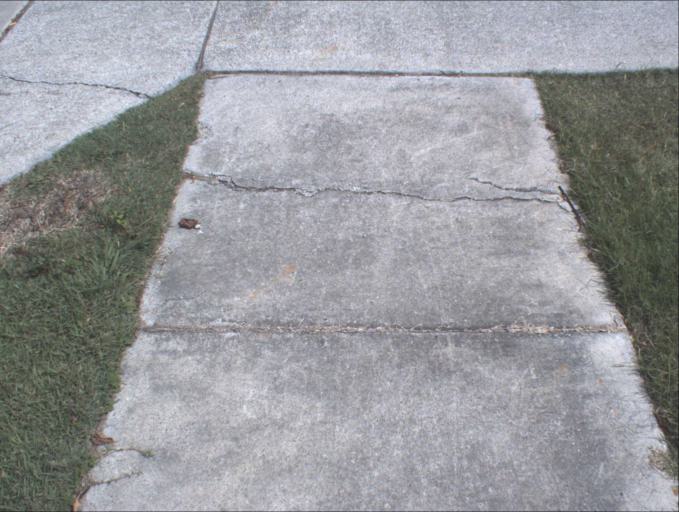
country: AU
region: Queensland
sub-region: Logan
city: Park Ridge South
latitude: -27.6731
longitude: 153.0274
